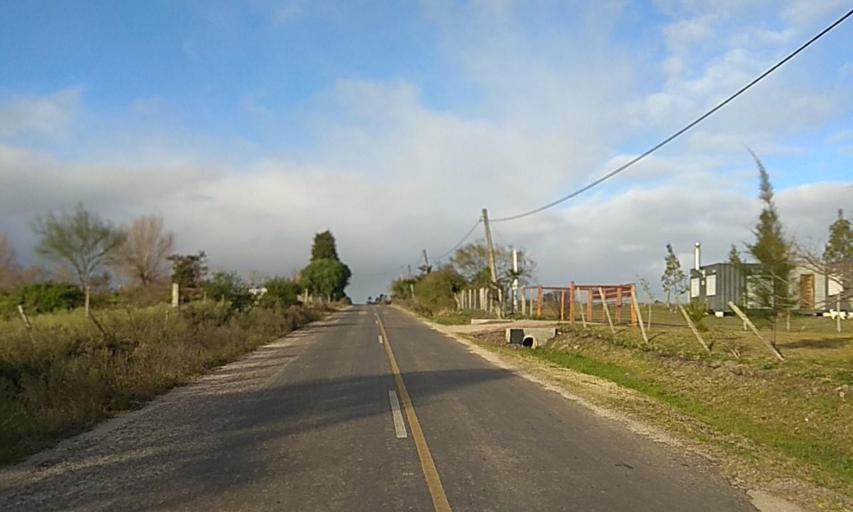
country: UY
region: Florida
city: Florida
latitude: -34.0449
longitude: -56.2002
